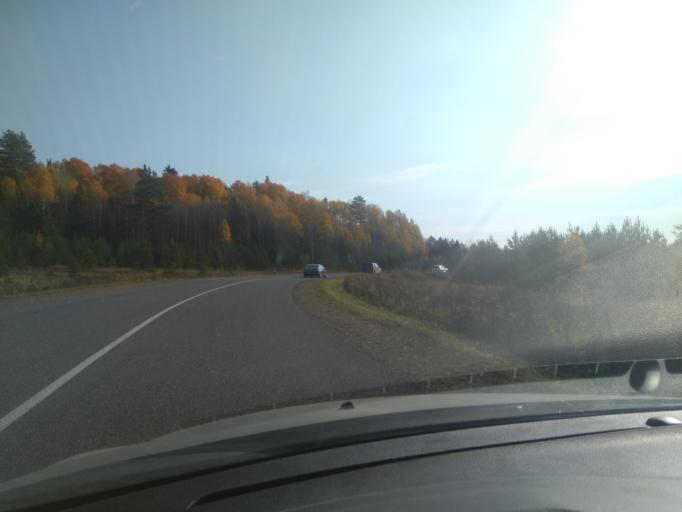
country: RU
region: Sverdlovsk
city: Mikhaylovsk
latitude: 56.5339
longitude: 59.2169
